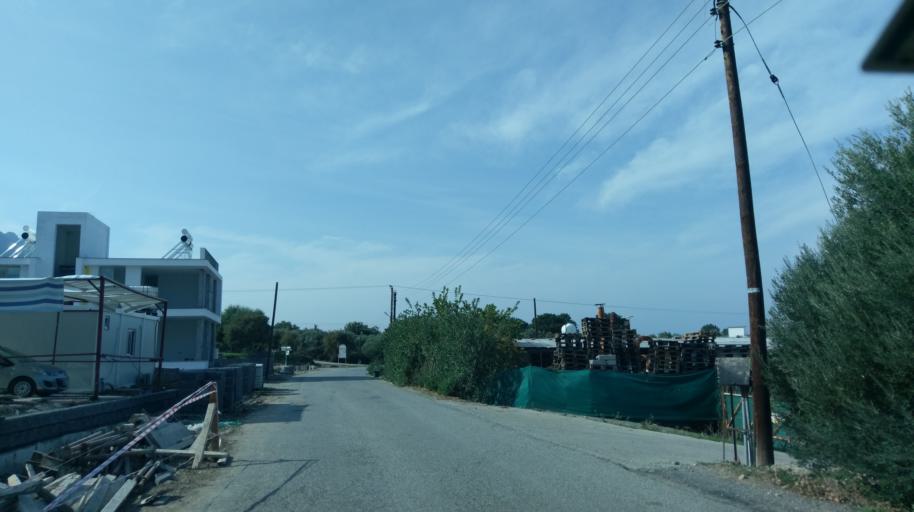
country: CY
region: Keryneia
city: Lapithos
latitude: 35.3473
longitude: 33.1548
